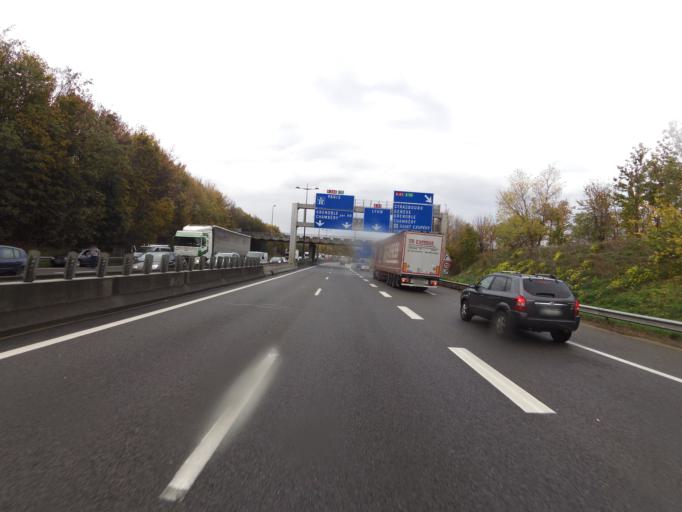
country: FR
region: Rhone-Alpes
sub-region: Departement du Rhone
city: Saint-Priest
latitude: 45.6979
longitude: 4.9686
